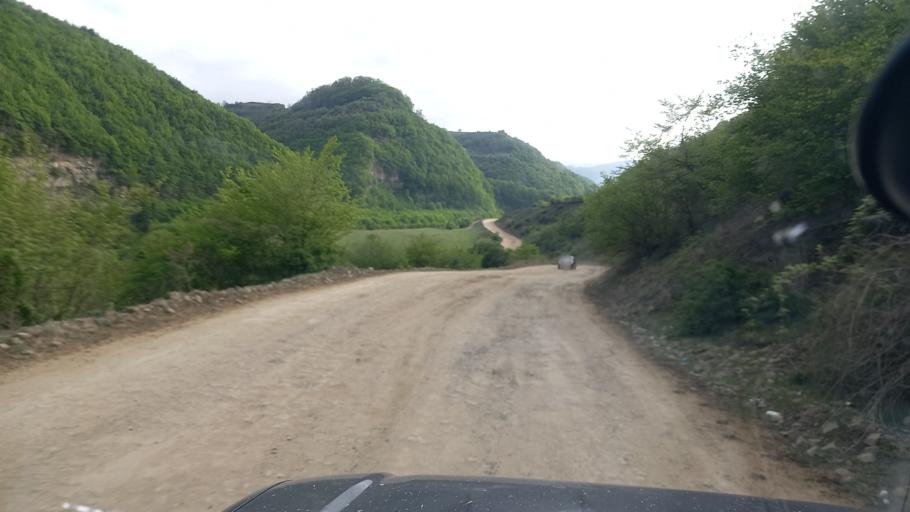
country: RU
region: Dagestan
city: Khuchni
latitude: 41.9652
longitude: 47.8728
